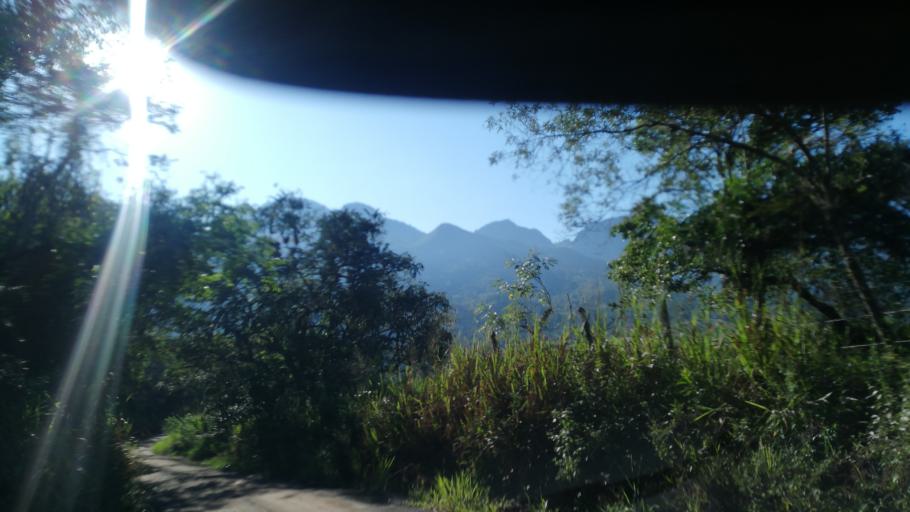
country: CO
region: Cundinamarca
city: Viani
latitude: 4.8358
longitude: -74.6214
